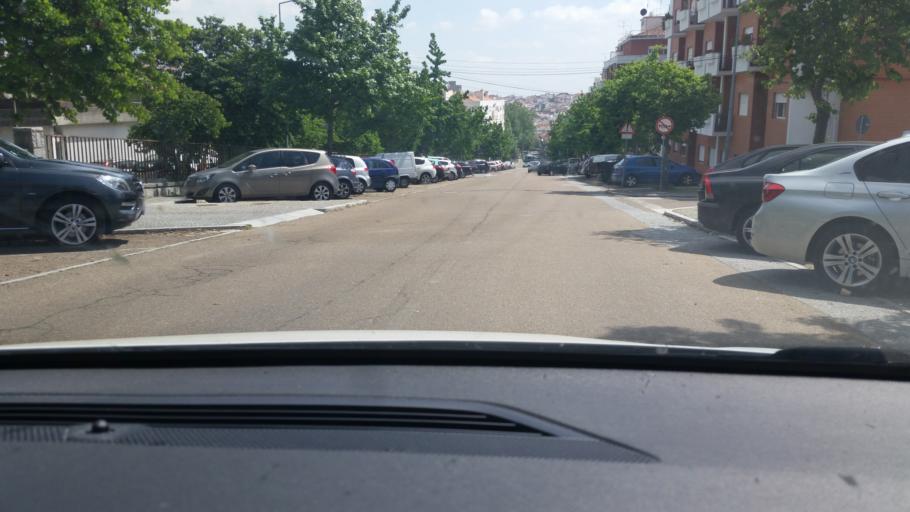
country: PT
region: Portalegre
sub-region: Portalegre
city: Portalegre
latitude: 39.3013
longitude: -7.4289
